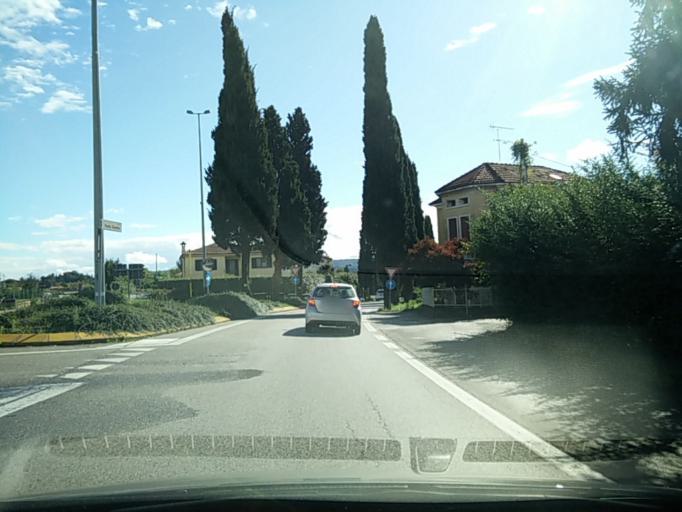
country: IT
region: Veneto
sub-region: Provincia di Treviso
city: Bigolino
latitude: 45.8639
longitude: 12.0222
